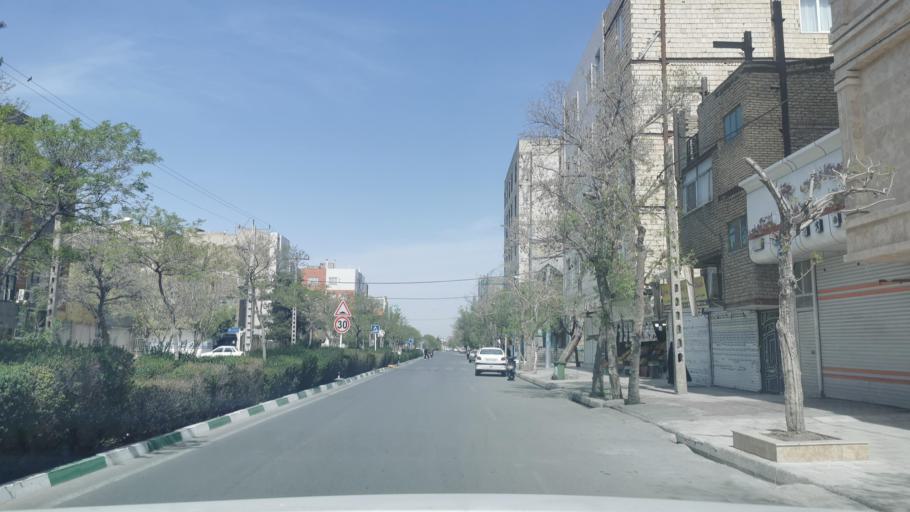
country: IR
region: Razavi Khorasan
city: Mashhad
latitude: 36.3198
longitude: 59.6242
